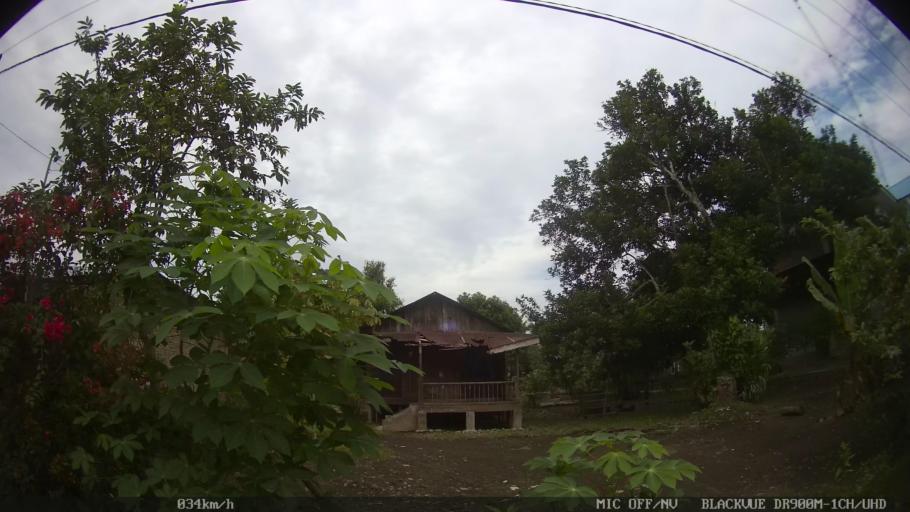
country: ID
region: North Sumatra
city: Sunggal
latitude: 3.6513
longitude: 98.5924
